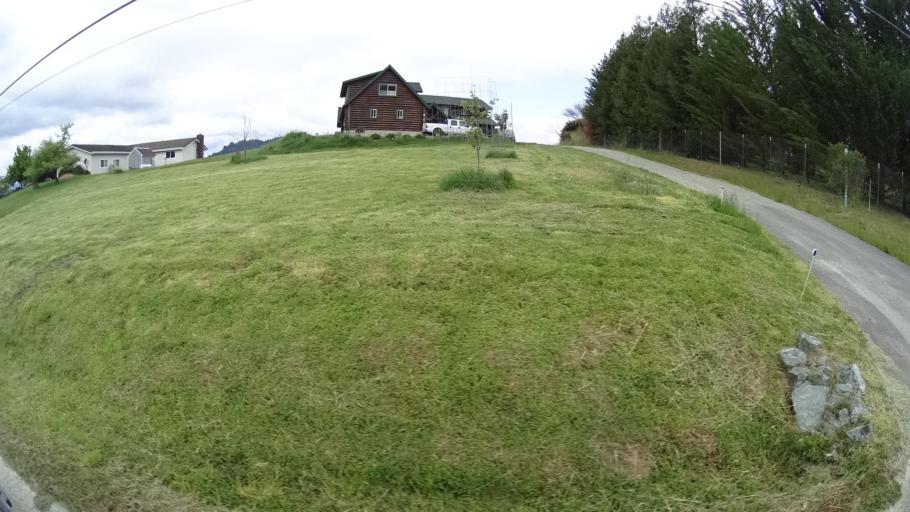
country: US
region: California
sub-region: Humboldt County
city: Redway
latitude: 40.1093
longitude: -123.7854
